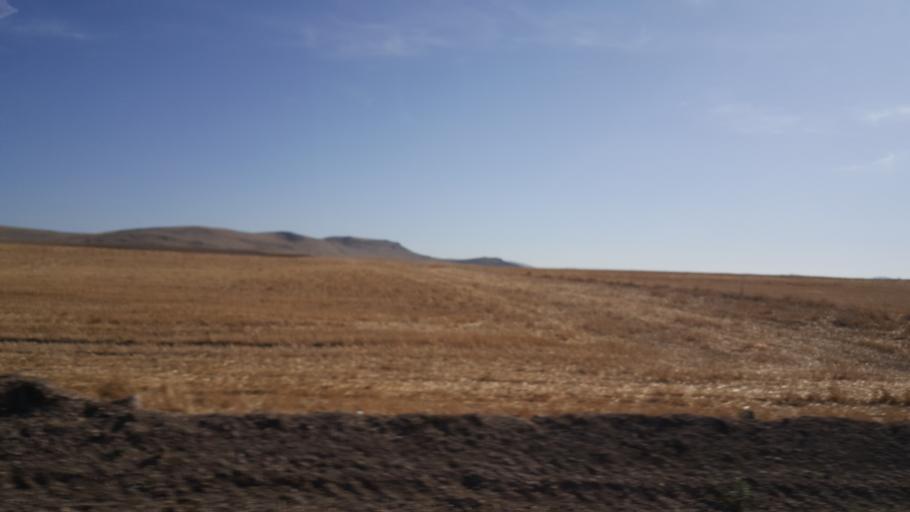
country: TR
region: Ankara
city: Yenice
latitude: 39.3529
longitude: 32.7816
